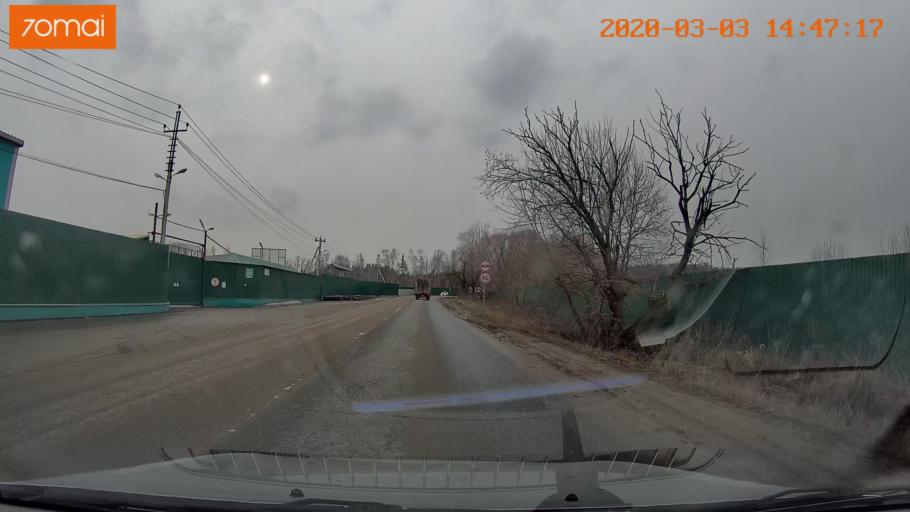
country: RU
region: Moskovskaya
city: Rodniki
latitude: 55.6927
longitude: 38.0489
